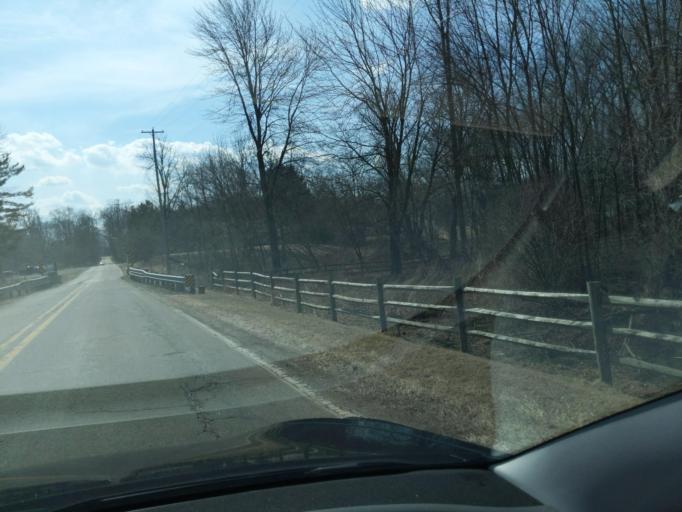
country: US
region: Michigan
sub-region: Livingston County
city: Pinckney
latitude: 42.4311
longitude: -84.0580
